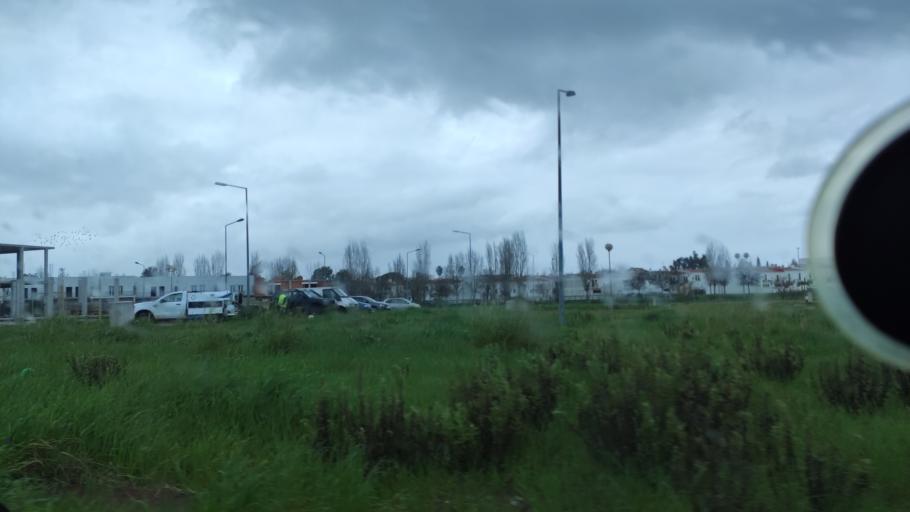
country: PT
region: Beja
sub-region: Beja
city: Beja
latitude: 38.0152
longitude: -7.8507
